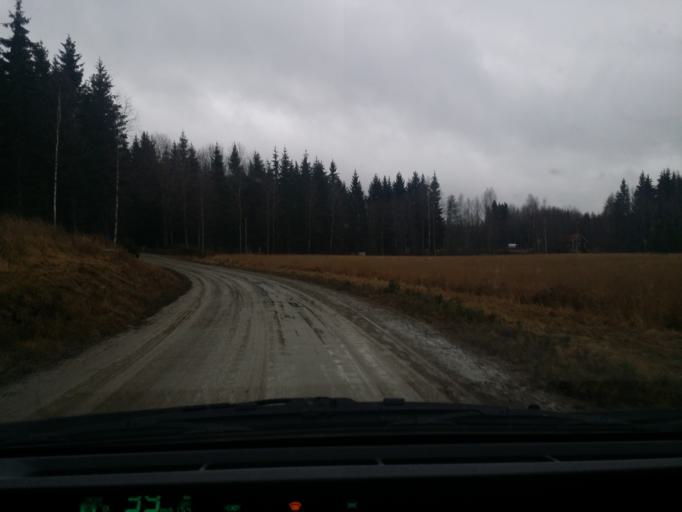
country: SE
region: Vaestmanland
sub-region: Vasteras
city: Skultuna
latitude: 59.7743
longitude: 16.3399
